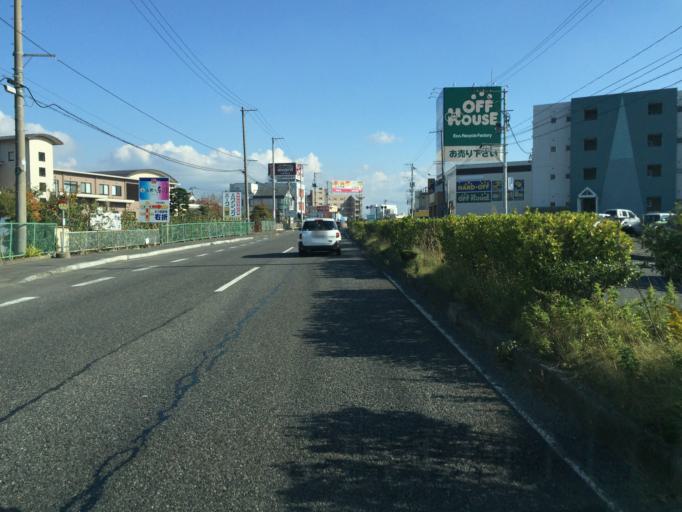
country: JP
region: Fukushima
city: Koriyama
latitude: 37.4112
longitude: 140.3483
